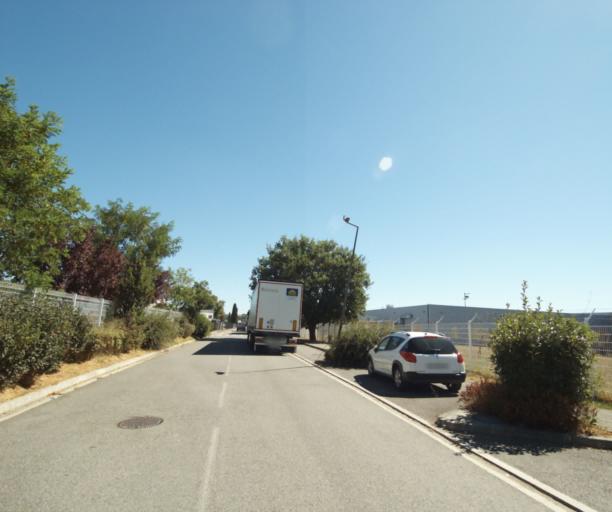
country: FR
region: Midi-Pyrenees
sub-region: Departement de la Haute-Garonne
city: Pechabou
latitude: 43.5102
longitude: 1.5191
